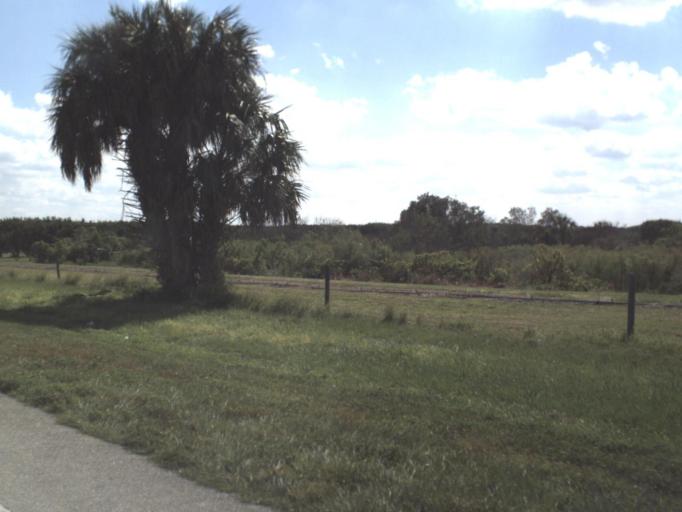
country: US
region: Florida
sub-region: Highlands County
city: Sebring
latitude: 27.4179
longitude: -81.5683
